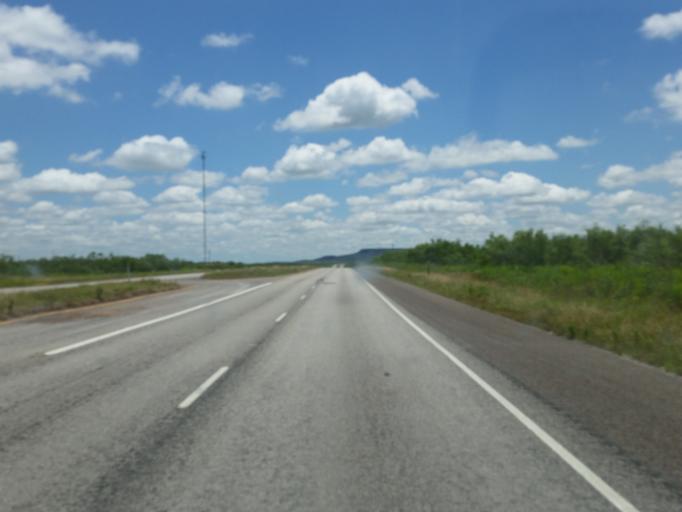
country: US
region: Texas
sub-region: Garza County
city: Post
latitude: 32.9867
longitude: -101.1331
